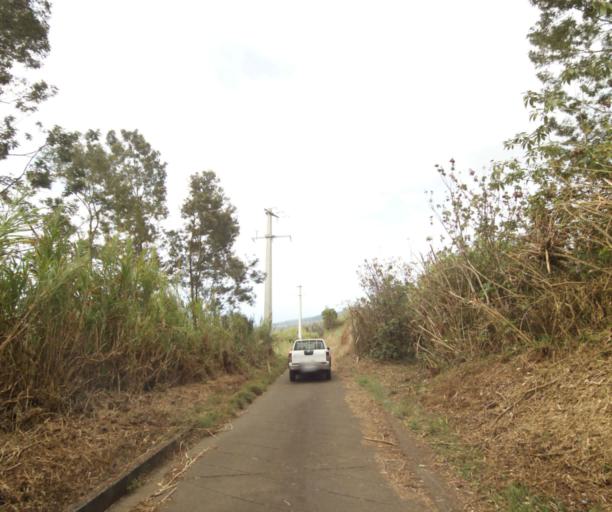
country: RE
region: Reunion
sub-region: Reunion
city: Saint-Paul
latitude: -21.0087
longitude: 55.3485
